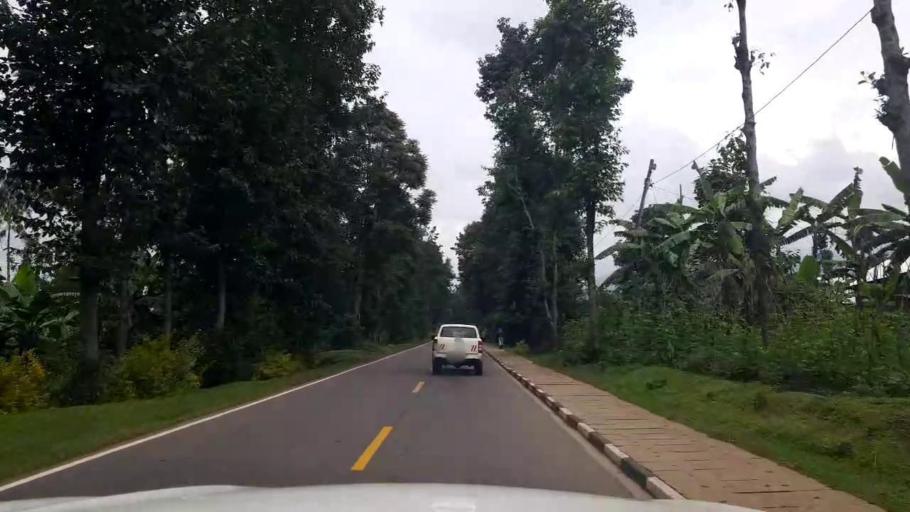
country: RW
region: Northern Province
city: Musanze
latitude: -1.4577
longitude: 29.6111
